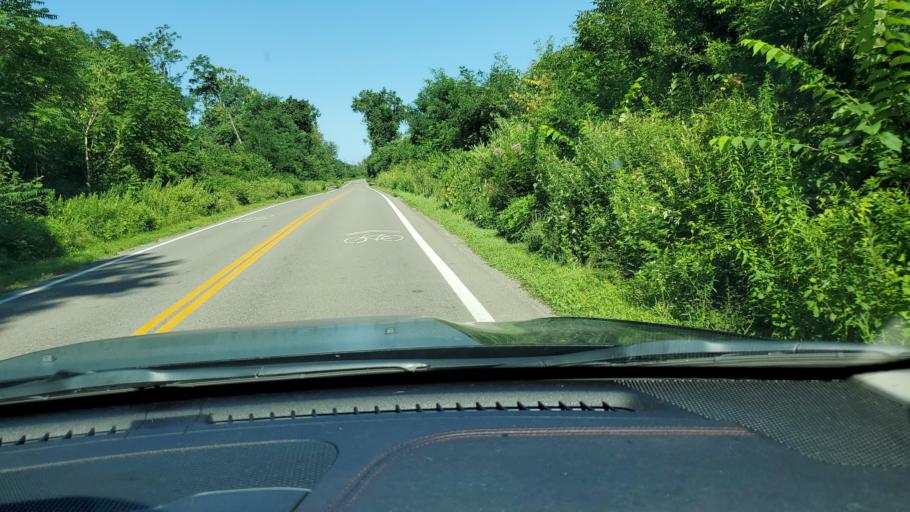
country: US
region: Ohio
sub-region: Mahoning County
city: Lowellville
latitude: 41.0494
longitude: -80.5642
